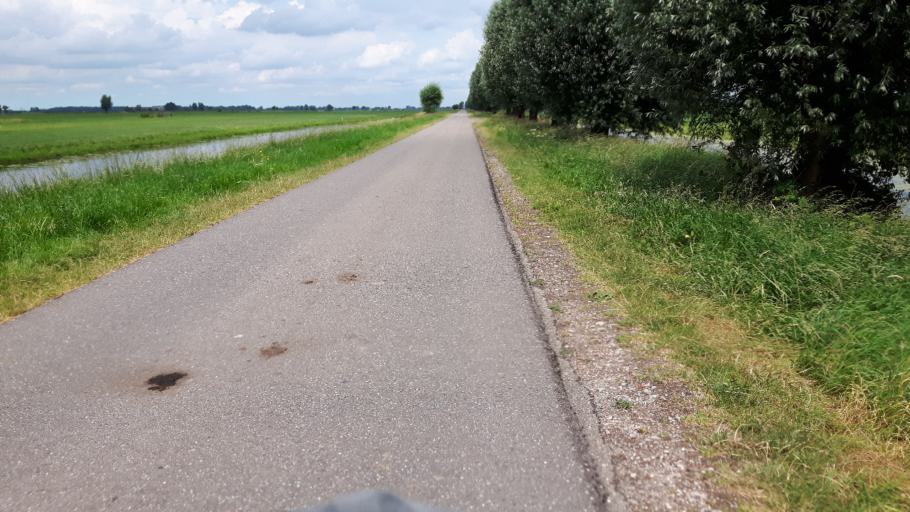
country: NL
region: South Holland
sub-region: Molenwaard
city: Nieuw-Lekkerland
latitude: 51.9046
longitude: 4.7255
